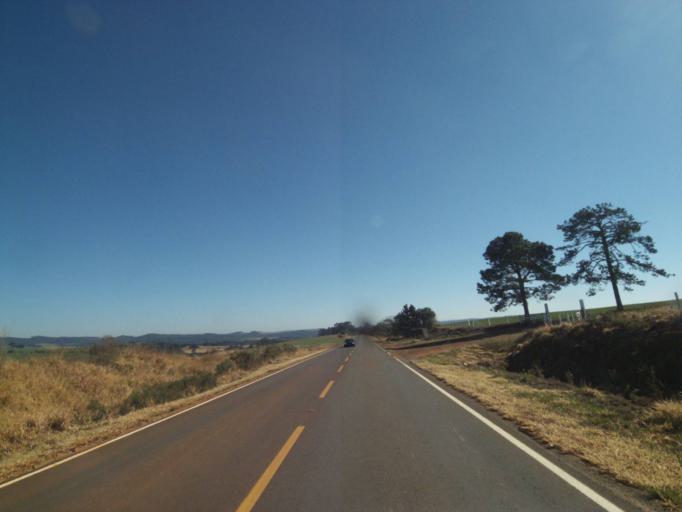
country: BR
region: Parana
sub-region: Tibagi
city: Tibagi
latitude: -24.4901
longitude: -50.4680
